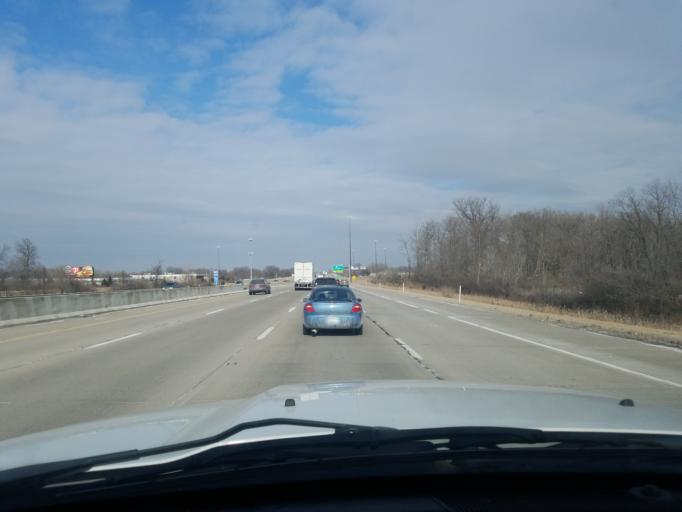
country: US
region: Indiana
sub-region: Marion County
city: Warren Park
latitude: 39.7459
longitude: -86.0375
